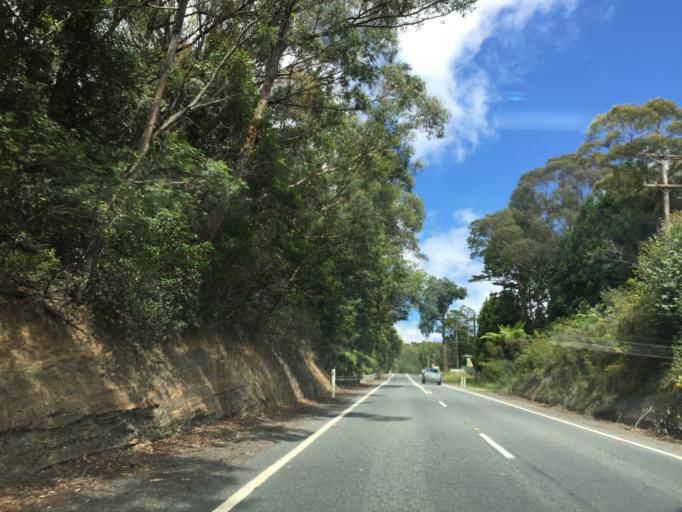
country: AU
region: New South Wales
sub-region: Blue Mountains Municipality
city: Hazelbrook
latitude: -33.5067
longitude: 150.5008
